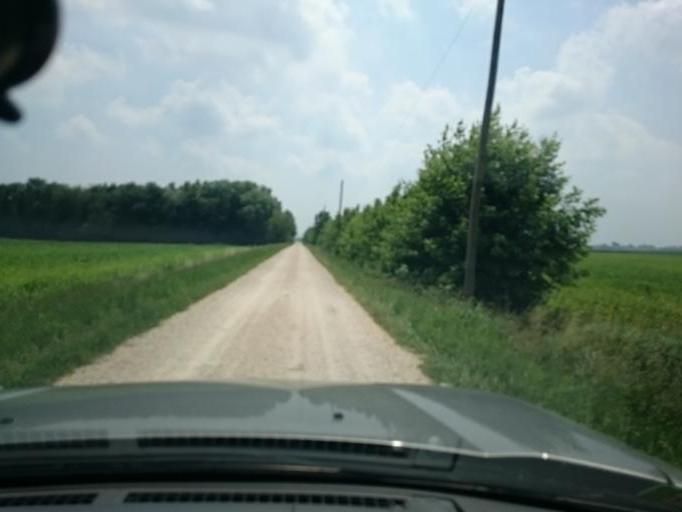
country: IT
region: Veneto
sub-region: Provincia di Padova
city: Arzergrande
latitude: 45.2584
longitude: 12.0534
